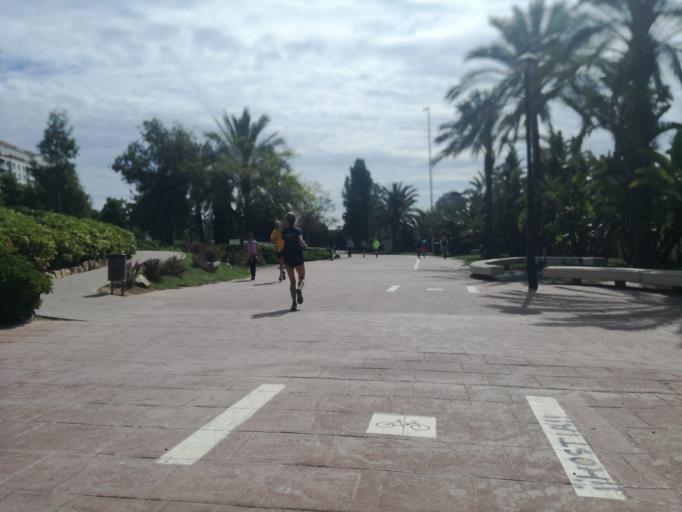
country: ES
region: Valencia
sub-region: Provincia de Valencia
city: Valencia
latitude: 39.4541
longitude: -0.3446
